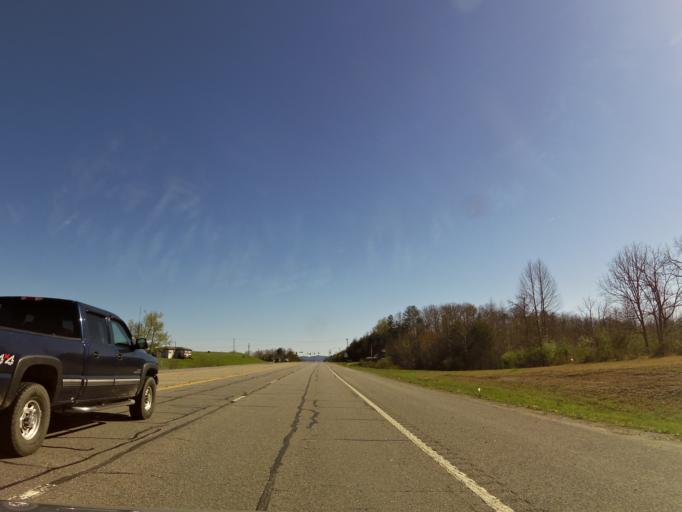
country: US
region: Tennessee
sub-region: Scott County
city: Huntsville
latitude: 36.4159
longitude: -84.5381
